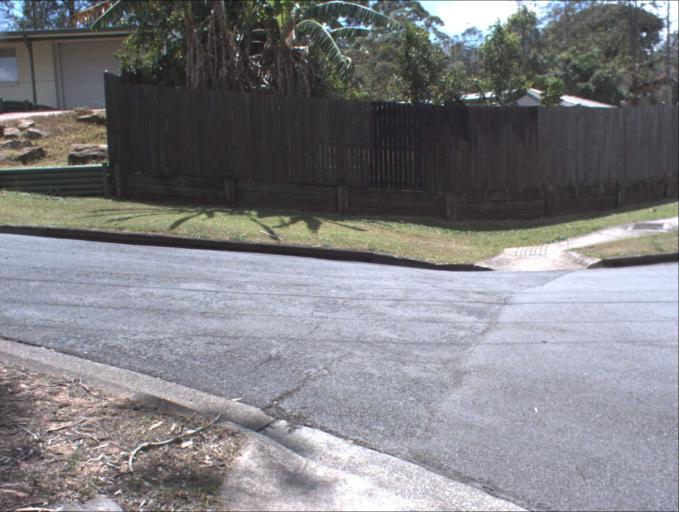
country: AU
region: Queensland
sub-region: Logan
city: Slacks Creek
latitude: -27.6413
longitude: 153.1678
